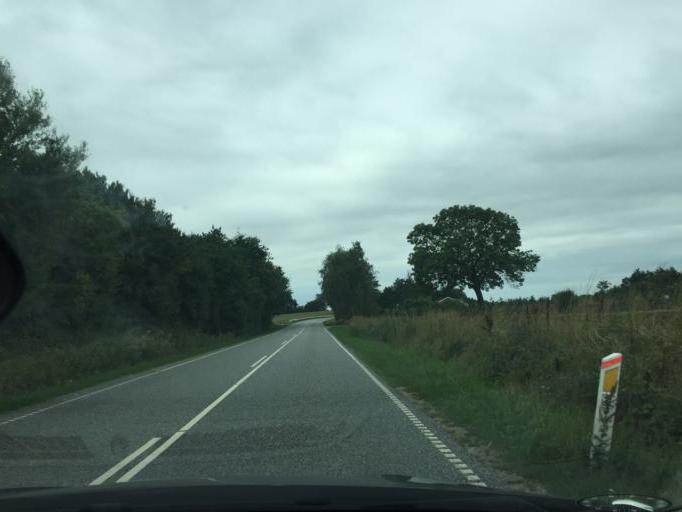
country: DK
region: South Denmark
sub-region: Assens Kommune
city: Vissenbjerg
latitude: 55.3666
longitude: 10.0916
